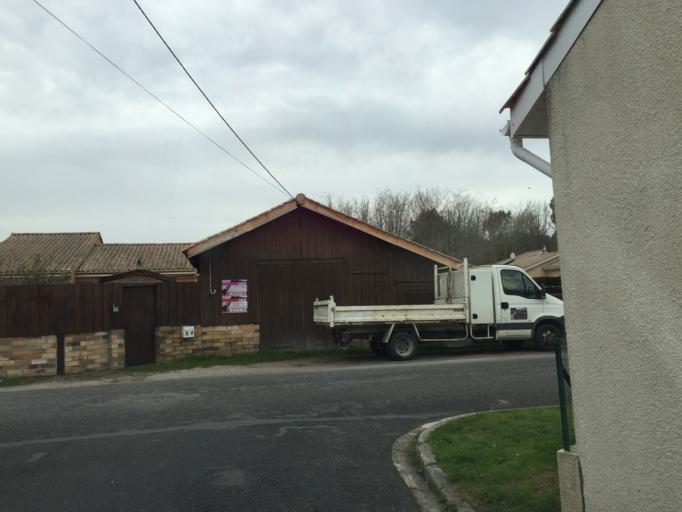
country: FR
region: Aquitaine
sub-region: Departement de la Gironde
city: Carcans
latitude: 45.0783
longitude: -1.0490
